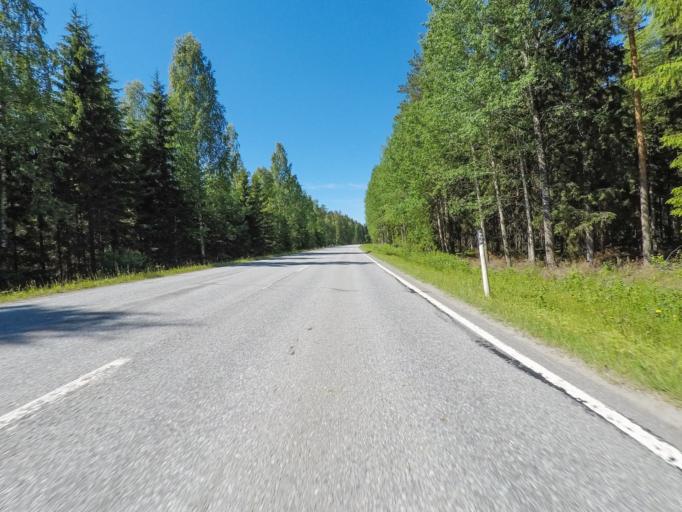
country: FI
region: Southern Savonia
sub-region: Savonlinna
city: Rantasalmi
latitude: 62.0154
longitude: 28.3822
